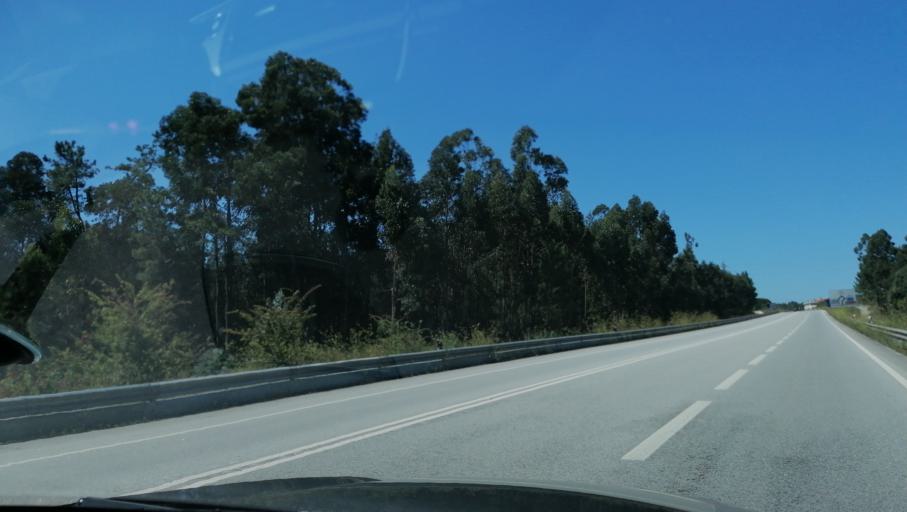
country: PT
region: Aveiro
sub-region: Agueda
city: Agueda
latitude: 40.5578
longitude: -8.4589
